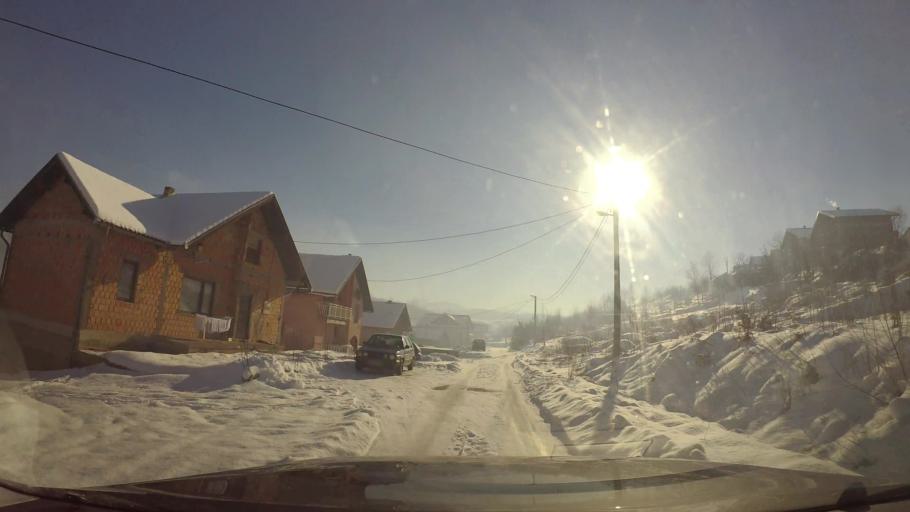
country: BA
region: Federation of Bosnia and Herzegovina
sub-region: Kanton Sarajevo
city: Sarajevo
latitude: 43.8182
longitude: 18.3732
